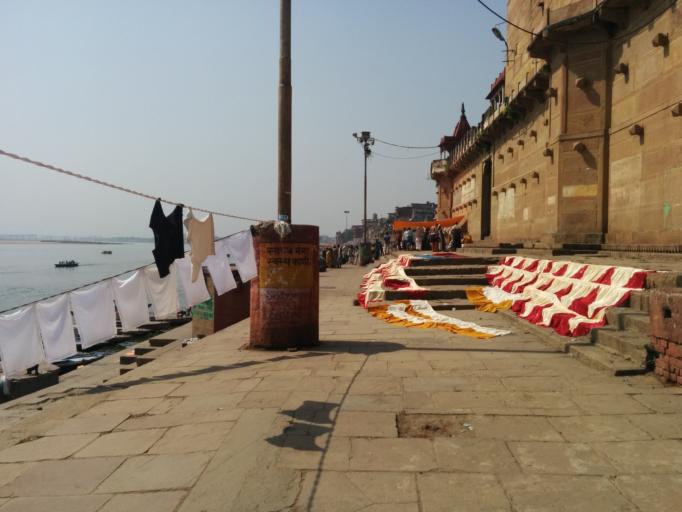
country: IN
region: Uttar Pradesh
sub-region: Varanasi
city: Varanasi
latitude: 25.3028
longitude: 83.0081
